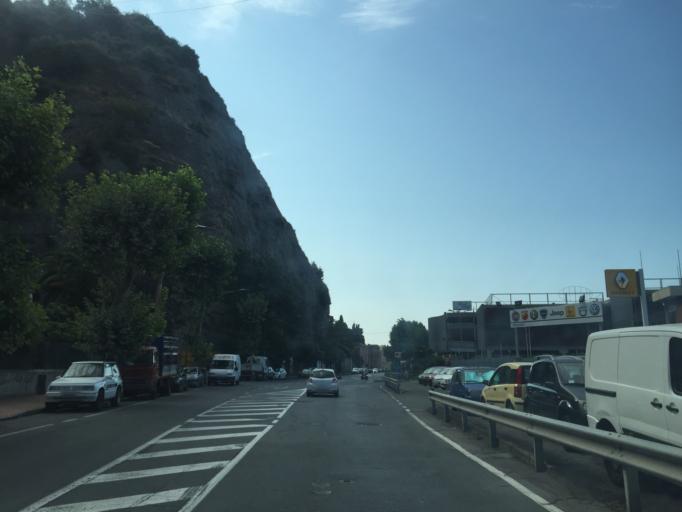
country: IT
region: Liguria
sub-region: Provincia di Imperia
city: Ventimiglia
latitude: 43.8014
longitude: 7.5992
